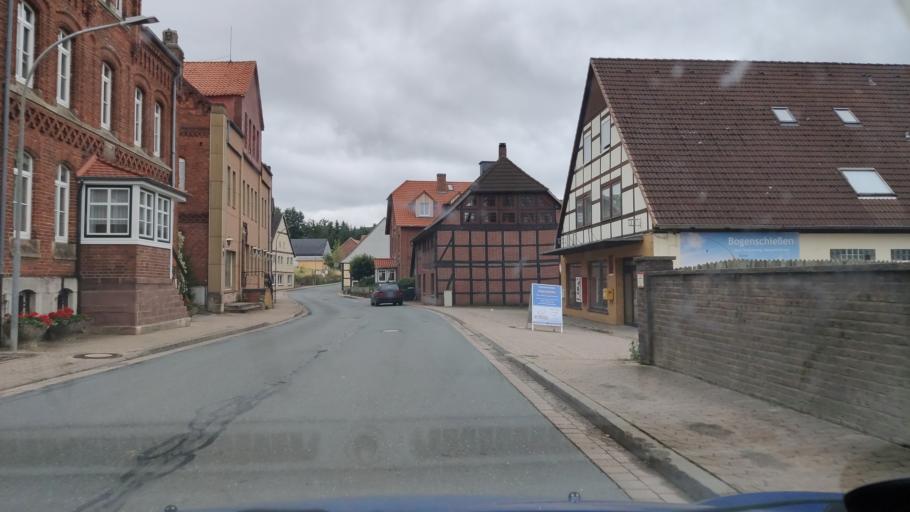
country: DE
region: Lower Saxony
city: Coppenbrugge
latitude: 52.0885
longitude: 9.4984
